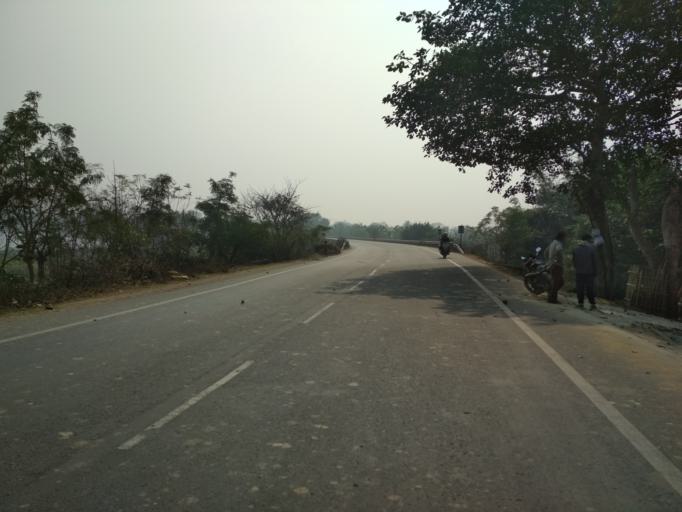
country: IN
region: Bihar
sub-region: Khagaria
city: Khagaria
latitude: 25.4962
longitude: 86.5951
